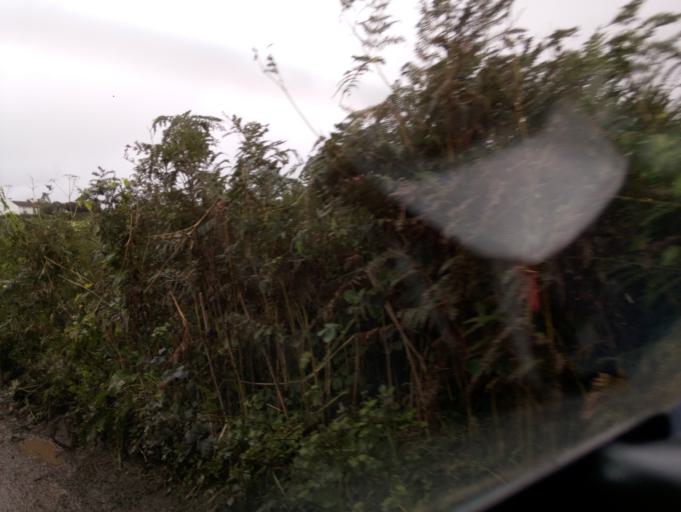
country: GB
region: England
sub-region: Devon
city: Dartmouth
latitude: 50.3568
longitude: -3.6453
